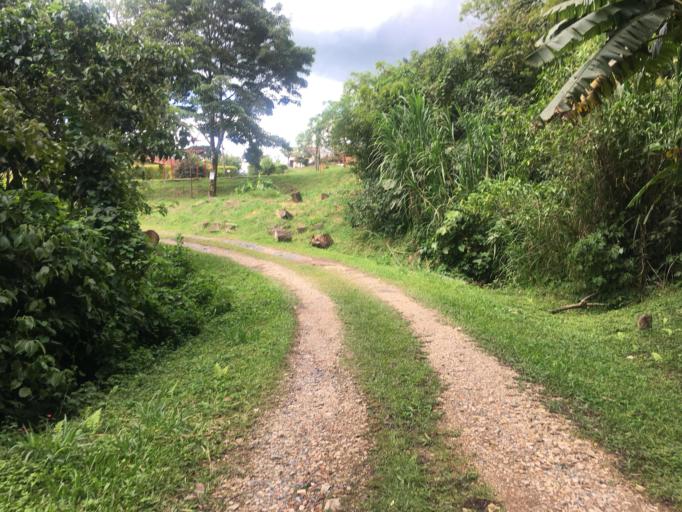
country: CO
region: Santander
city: Barbosa
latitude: 5.9182
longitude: -73.6051
